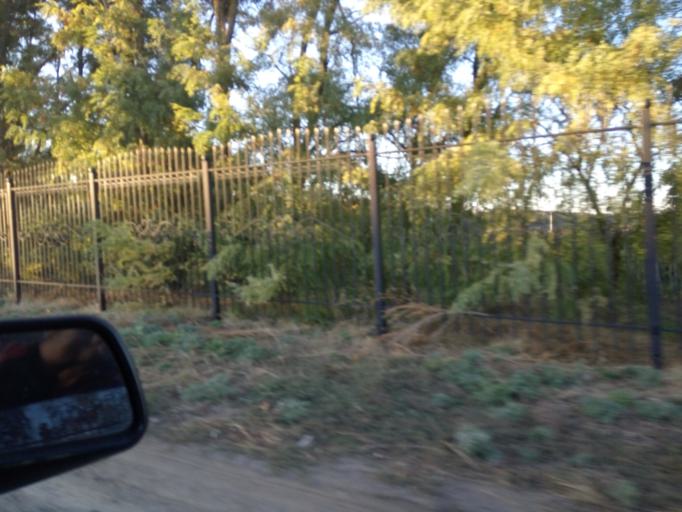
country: RU
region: Rostov
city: Temernik
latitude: 47.3575
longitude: 39.7425
